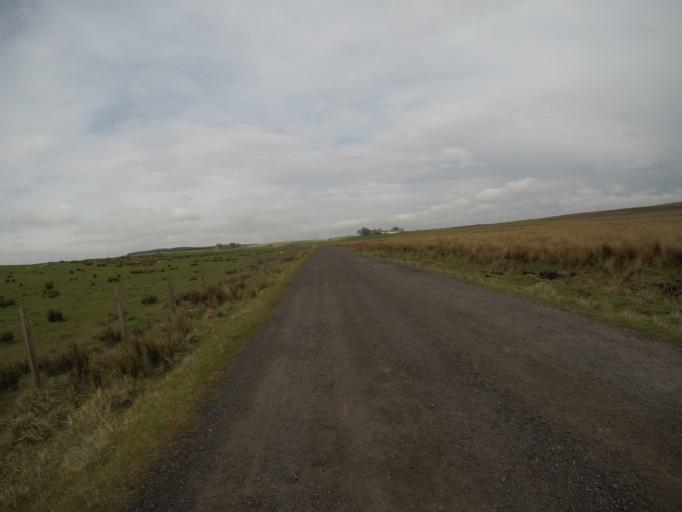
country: GB
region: Scotland
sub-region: East Ayrshire
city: Galston
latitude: 55.6860
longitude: -4.3986
